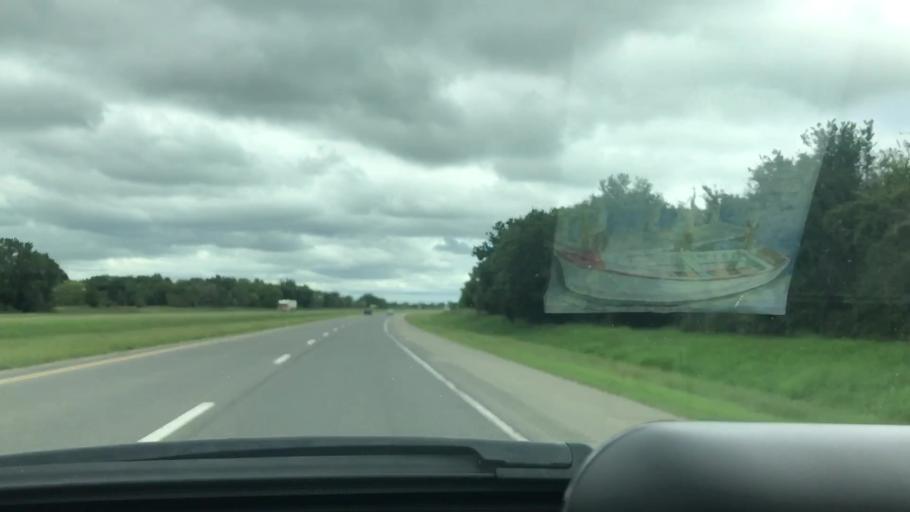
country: US
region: Oklahoma
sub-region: McIntosh County
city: Checotah
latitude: 35.5844
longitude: -95.4899
